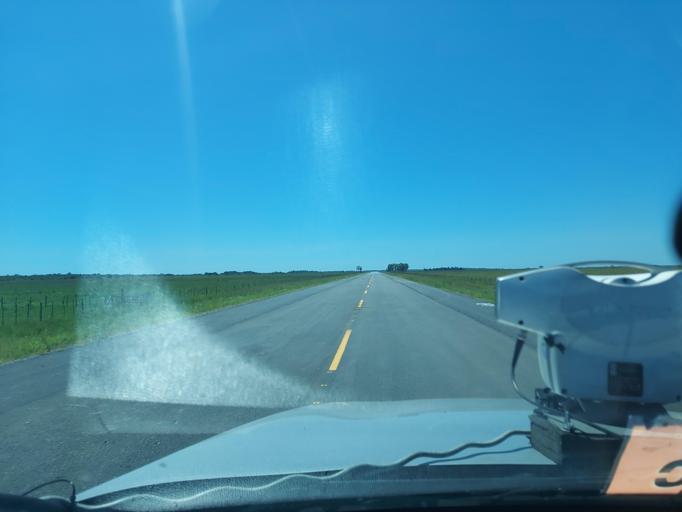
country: PY
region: Neembucu
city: Pilar
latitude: -26.8193
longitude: -58.2532
